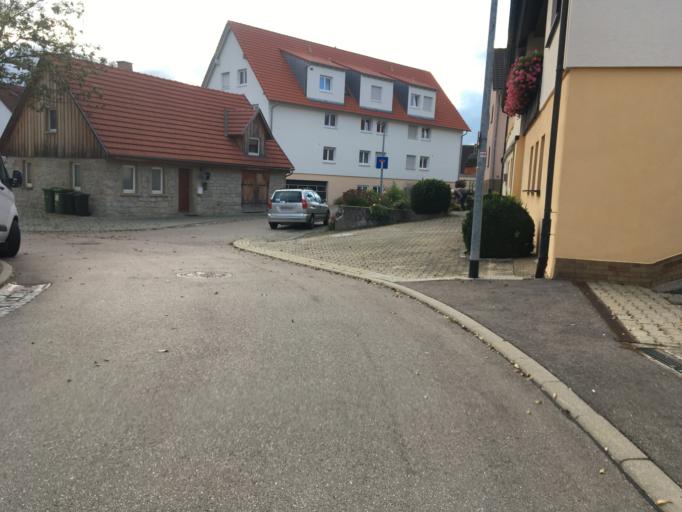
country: DE
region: Baden-Wuerttemberg
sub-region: Regierungsbezirk Stuttgart
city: Kuenzelsau
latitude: 49.2572
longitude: 9.6855
